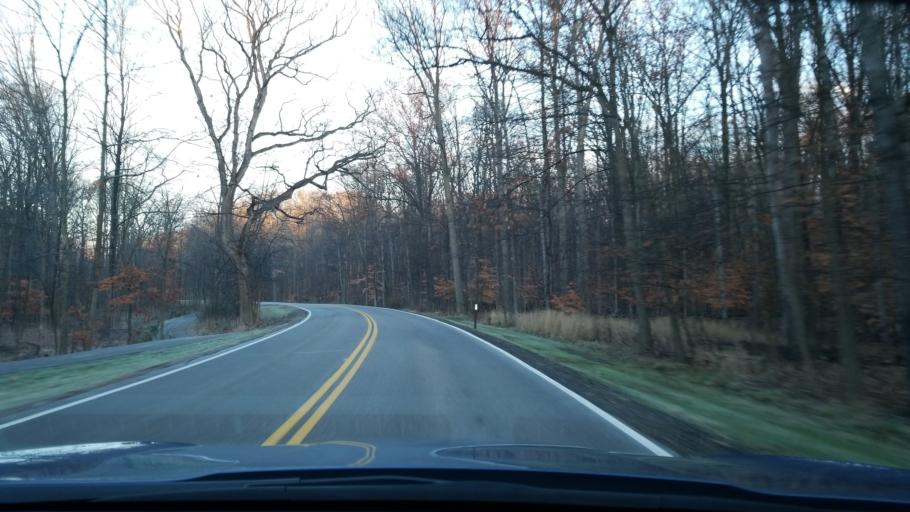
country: US
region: Ohio
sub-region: Cuyahoga County
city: Middleburg Heights
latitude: 41.3460
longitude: -81.8350
